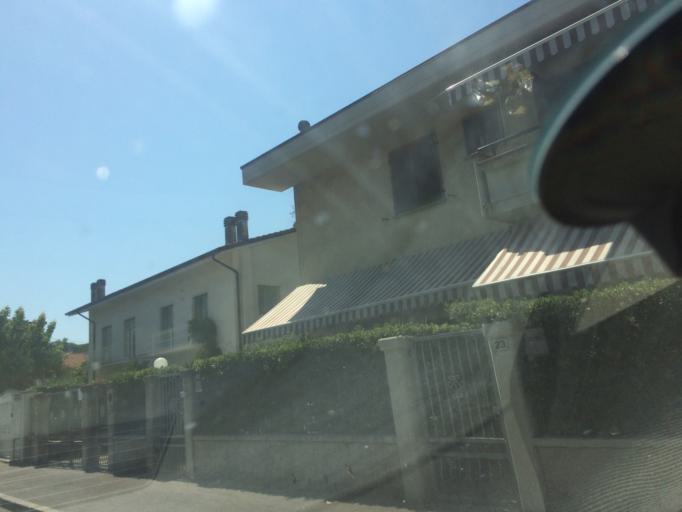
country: IT
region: Tuscany
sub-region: Provincia di Massa-Carrara
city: Massa
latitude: 44.0126
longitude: 10.0957
